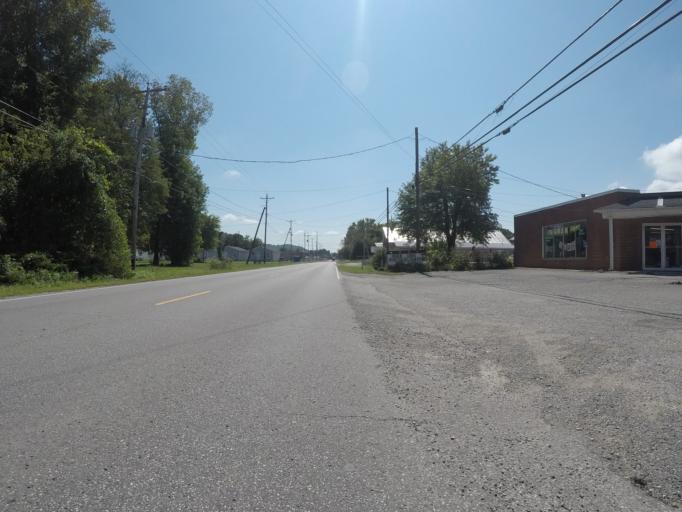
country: US
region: Kentucky
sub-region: Boyd County
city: Ashland
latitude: 38.4662
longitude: -82.6030
